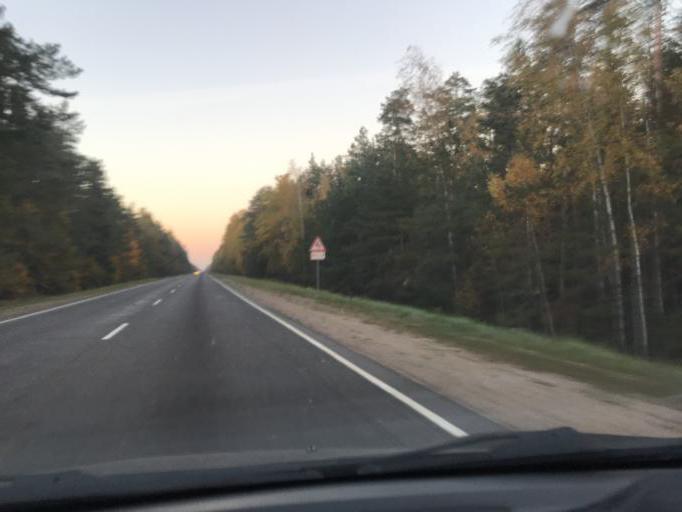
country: BY
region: Mogilev
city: Babruysk
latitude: 53.1183
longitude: 29.0530
